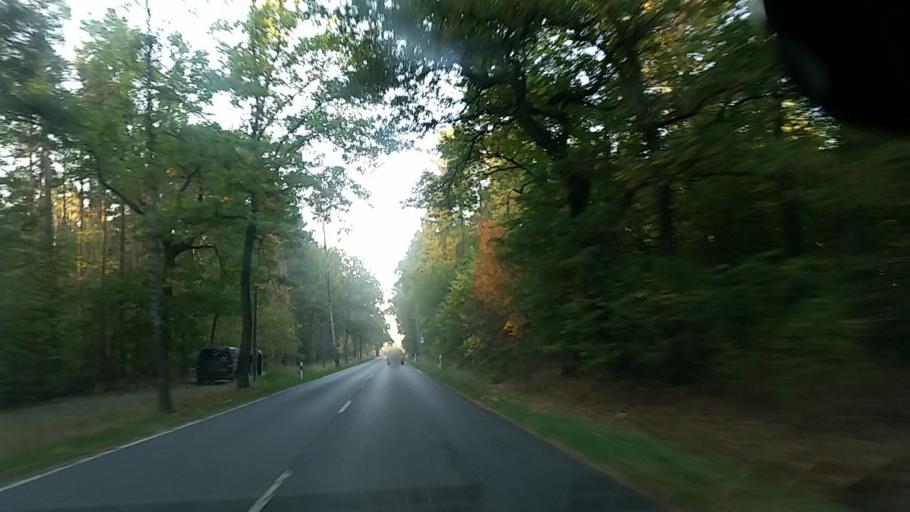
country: DE
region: Lower Saxony
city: Wolfsburg
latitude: 52.4595
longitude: 10.7844
